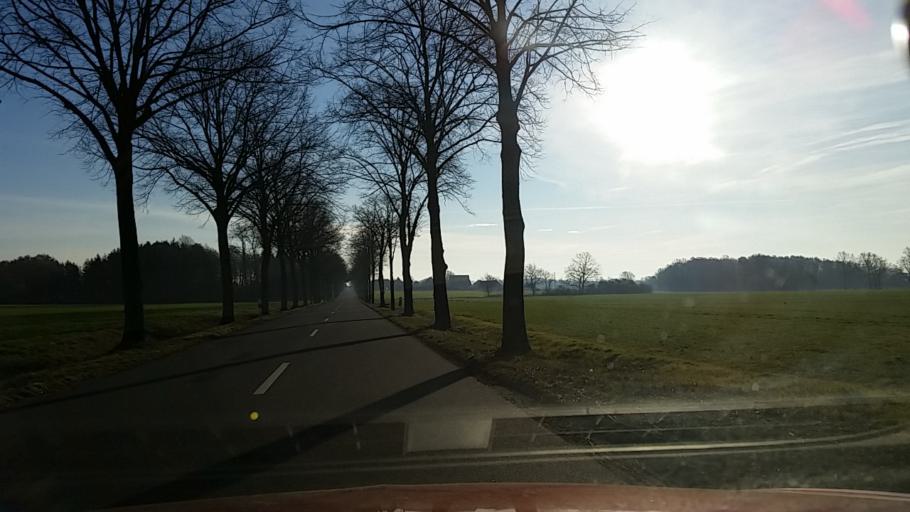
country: DE
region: Lower Saxony
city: Tiddische
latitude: 52.4875
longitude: 10.8287
